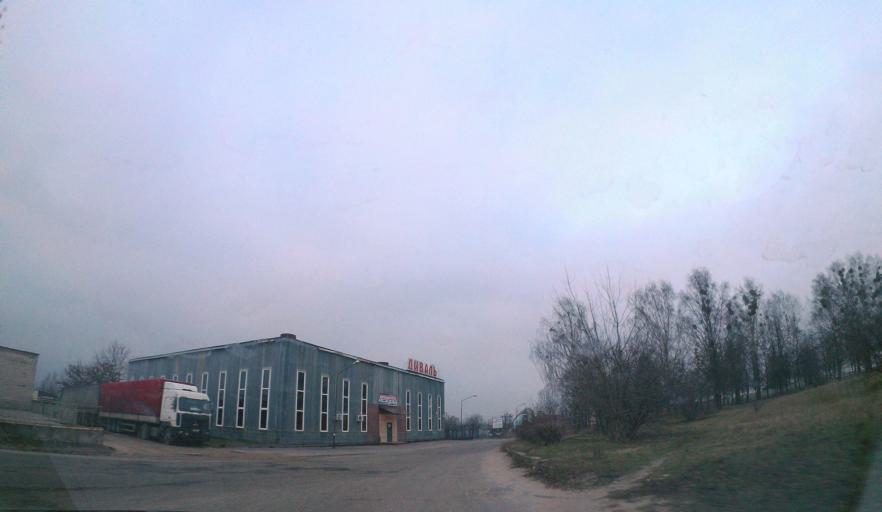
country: BY
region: Grodnenskaya
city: Hrodna
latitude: 53.6533
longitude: 23.8071
